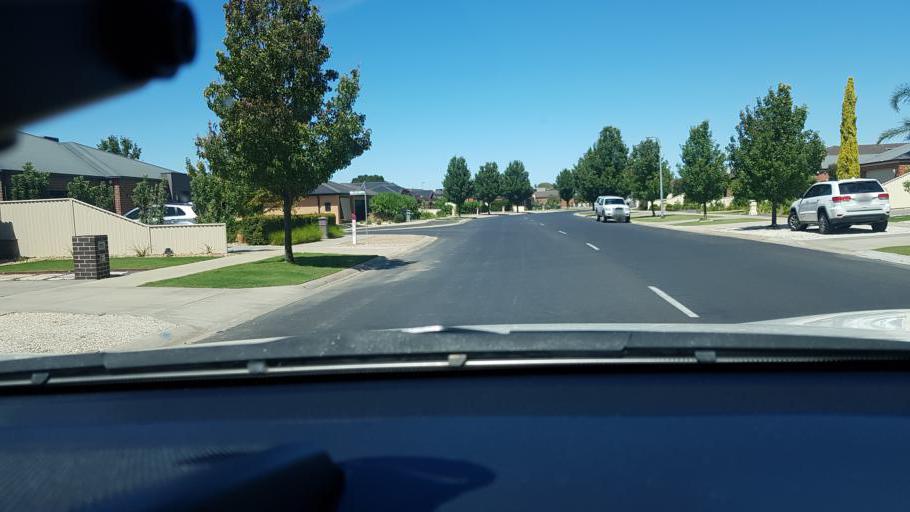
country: AU
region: Victoria
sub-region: Horsham
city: Horsham
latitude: -36.7135
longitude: 142.1794
